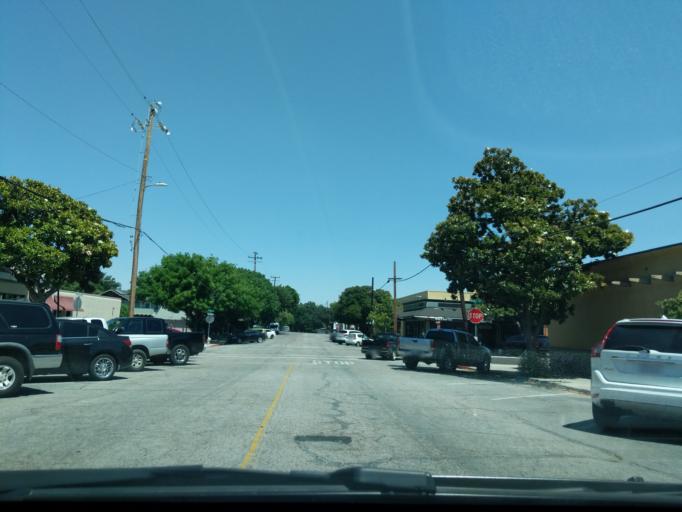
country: US
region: California
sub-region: San Luis Obispo County
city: Paso Robles
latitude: 35.6288
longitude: -120.6908
